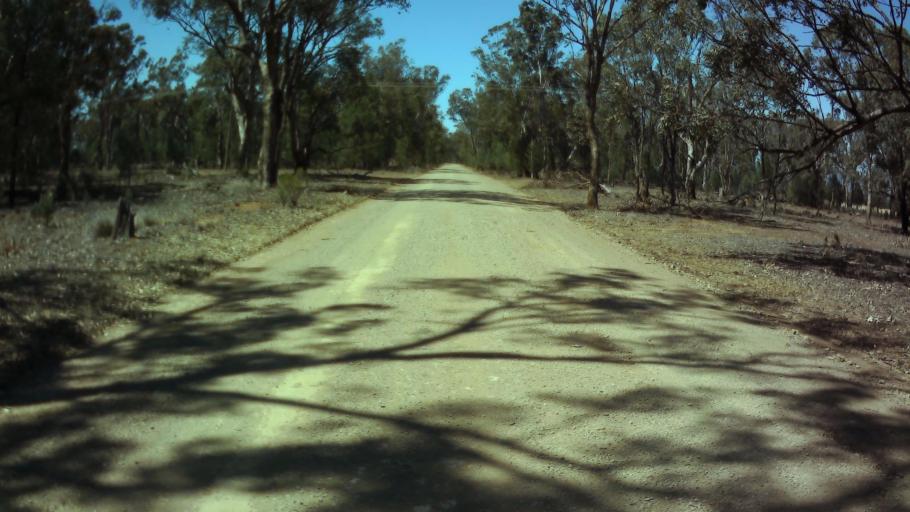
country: AU
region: New South Wales
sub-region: Weddin
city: Grenfell
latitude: -33.8538
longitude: 148.0877
